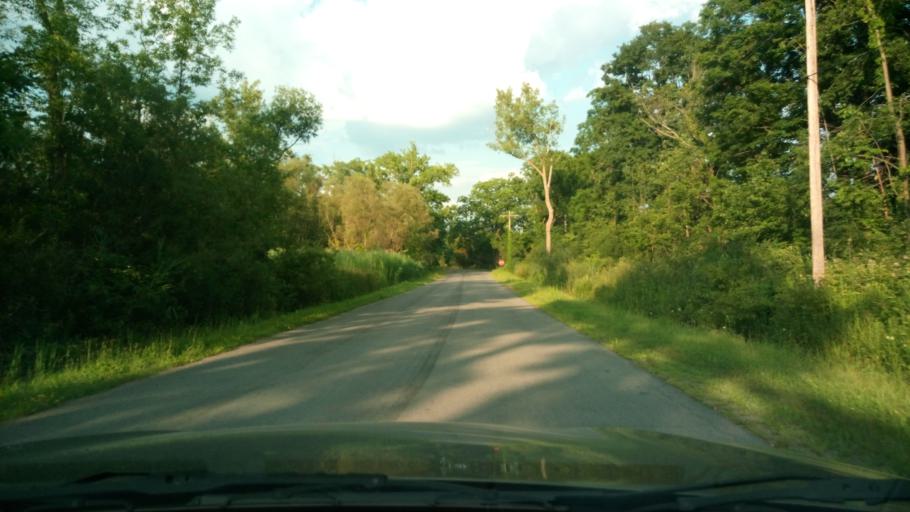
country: US
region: New York
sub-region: Wayne County
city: Lyons
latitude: 43.0761
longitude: -76.9487
